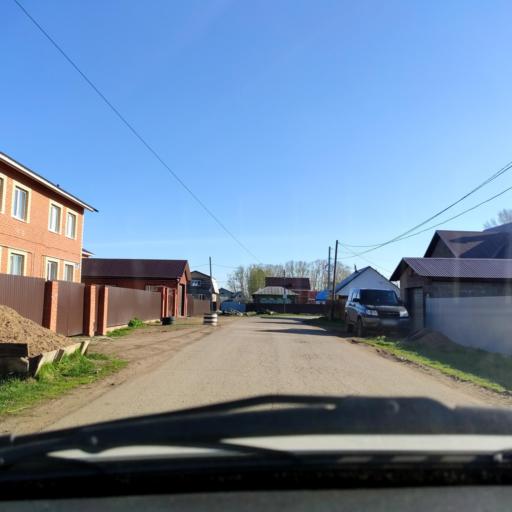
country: RU
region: Bashkortostan
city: Mikhaylovka
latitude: 54.7787
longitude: 55.8284
